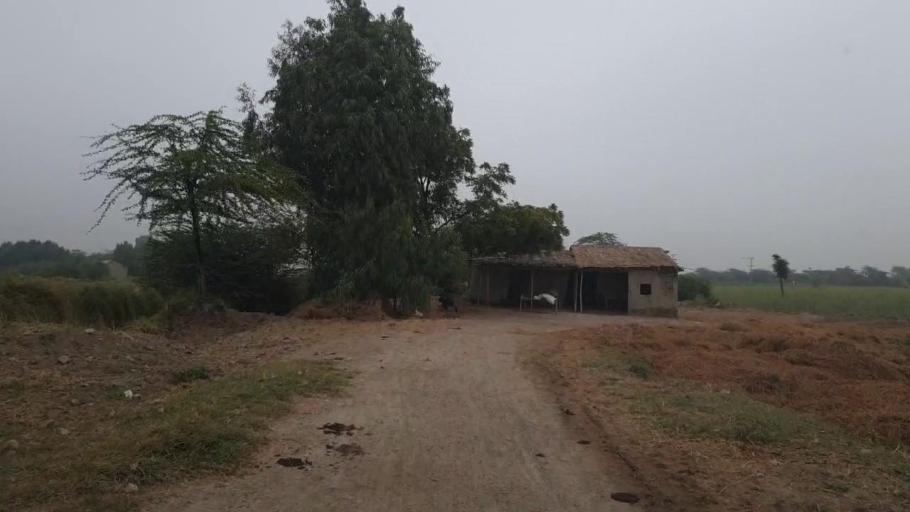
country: PK
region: Sindh
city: Badin
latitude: 24.6213
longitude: 68.6917
